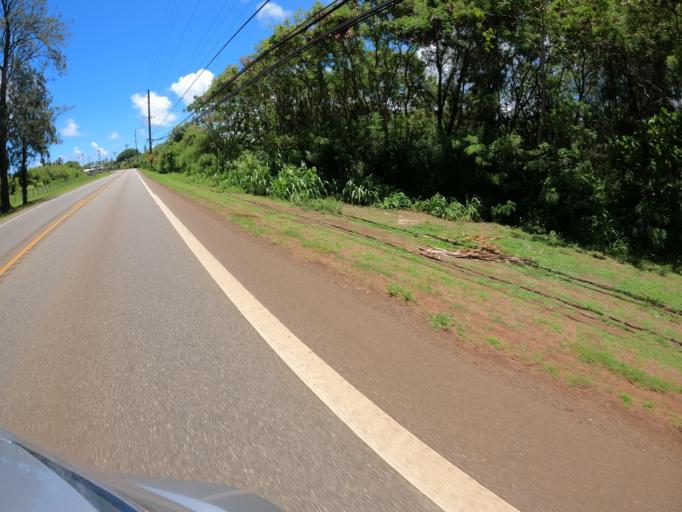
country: US
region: Hawaii
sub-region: Honolulu County
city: Kahuku
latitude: 21.6792
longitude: -157.9550
